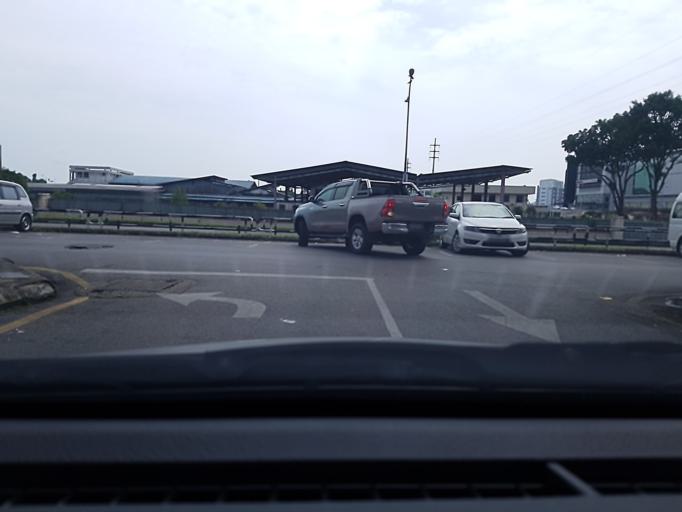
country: MY
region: Sarawak
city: Kuching
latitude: 1.5086
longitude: 110.3348
